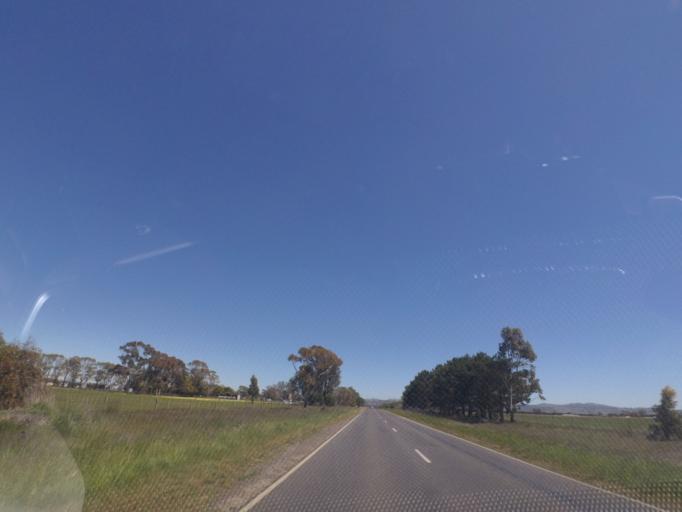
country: AU
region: Victoria
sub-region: Whittlesea
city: Whittlesea
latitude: -37.2911
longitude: 144.9072
